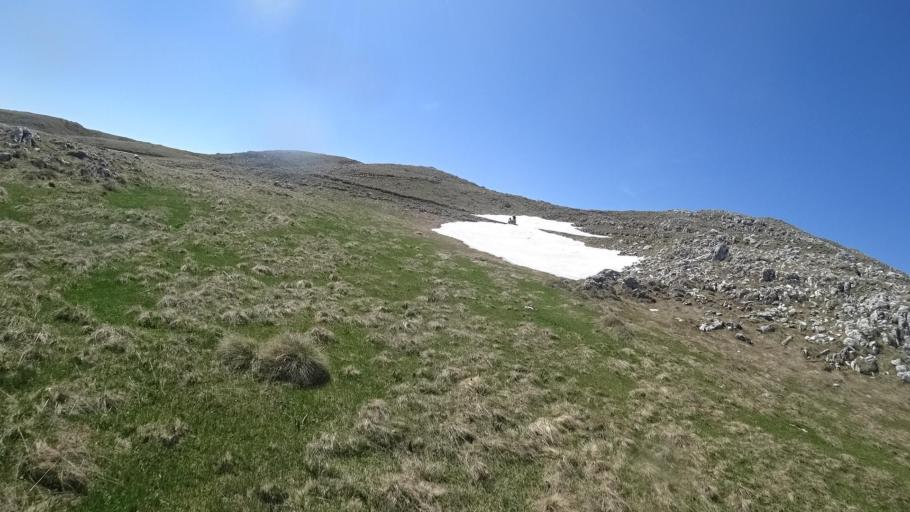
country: BA
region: Federation of Bosnia and Herzegovina
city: Travnik
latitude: 44.2853
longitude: 17.6389
